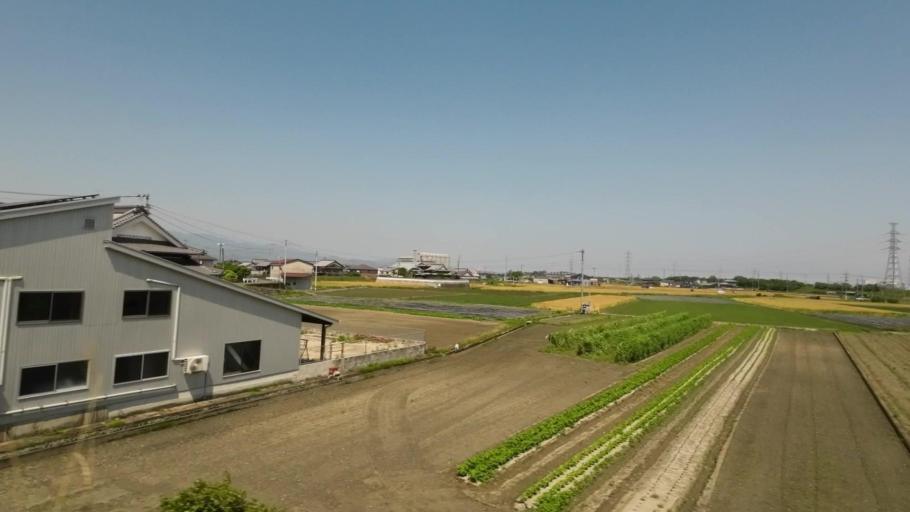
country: JP
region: Ehime
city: Saijo
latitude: 33.9027
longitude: 133.1769
